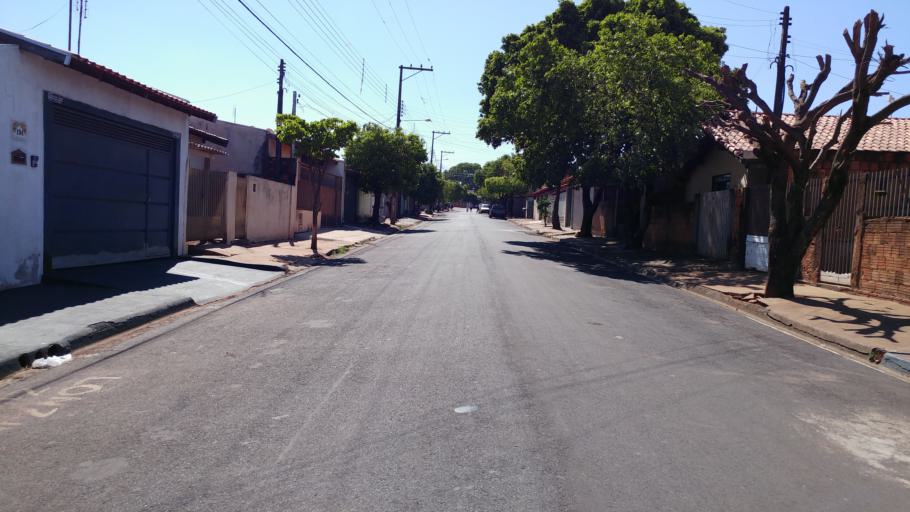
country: BR
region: Sao Paulo
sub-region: Paraguacu Paulista
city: Paraguacu Paulista
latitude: -22.4380
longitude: -50.5817
